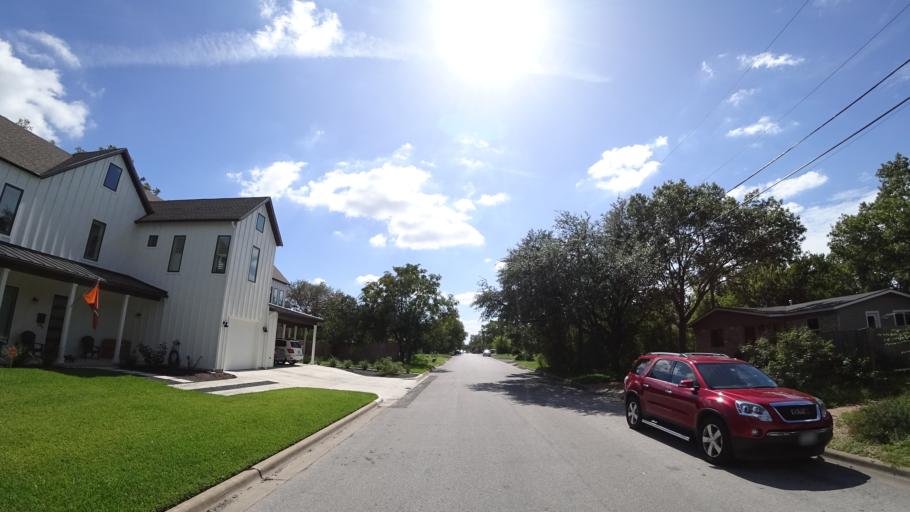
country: US
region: Texas
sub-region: Travis County
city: Austin
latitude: 30.3473
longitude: -97.7321
